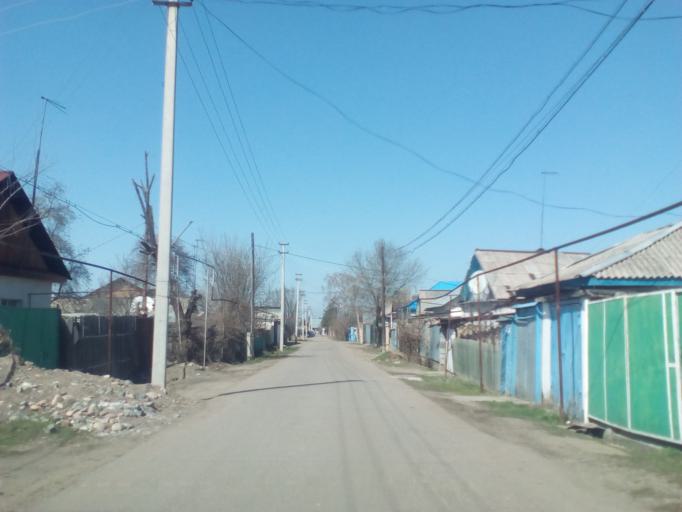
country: KZ
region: Almaty Oblysy
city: Burunday
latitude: 43.1601
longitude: 76.4085
